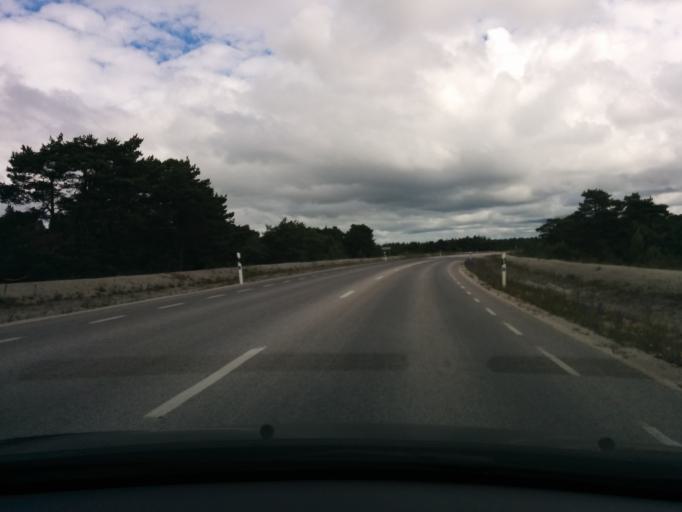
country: SE
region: Gotland
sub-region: Gotland
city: Visby
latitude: 57.6349
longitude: 18.3601
